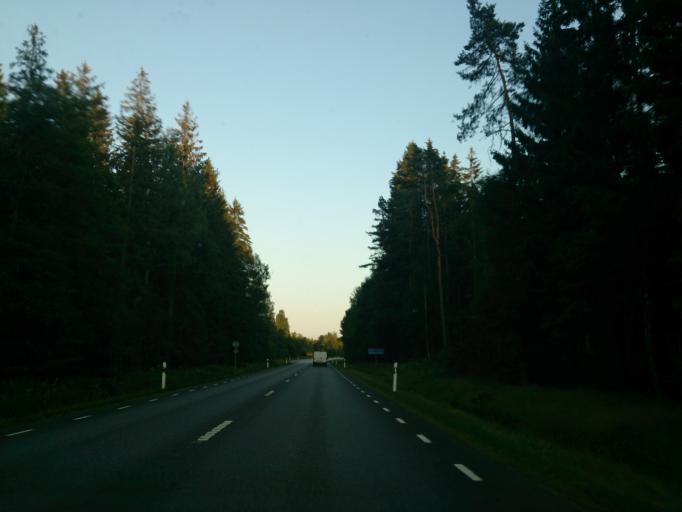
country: SE
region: Joenkoeping
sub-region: Varnamo Kommun
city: Rydaholm
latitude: 56.9902
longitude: 14.2963
